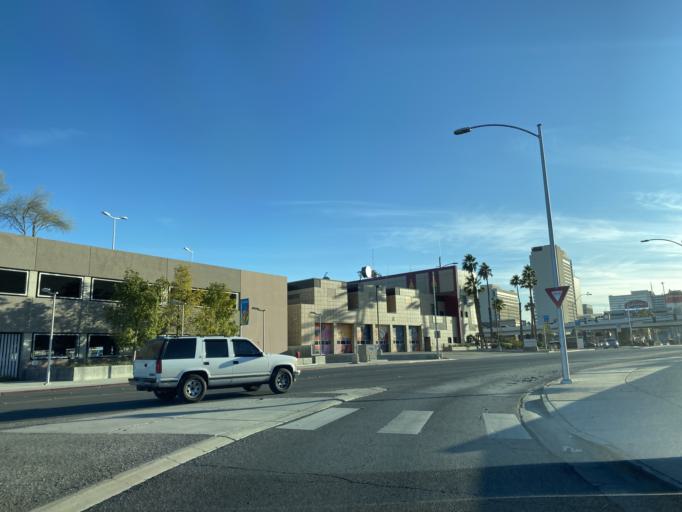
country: US
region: Nevada
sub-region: Clark County
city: Las Vegas
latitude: 36.1761
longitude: -115.1407
